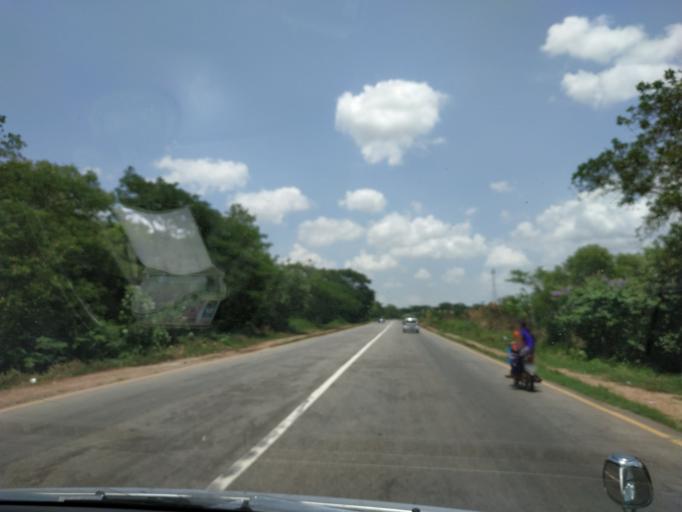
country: MM
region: Bago
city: Thanatpin
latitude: 17.4492
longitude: 96.6226
